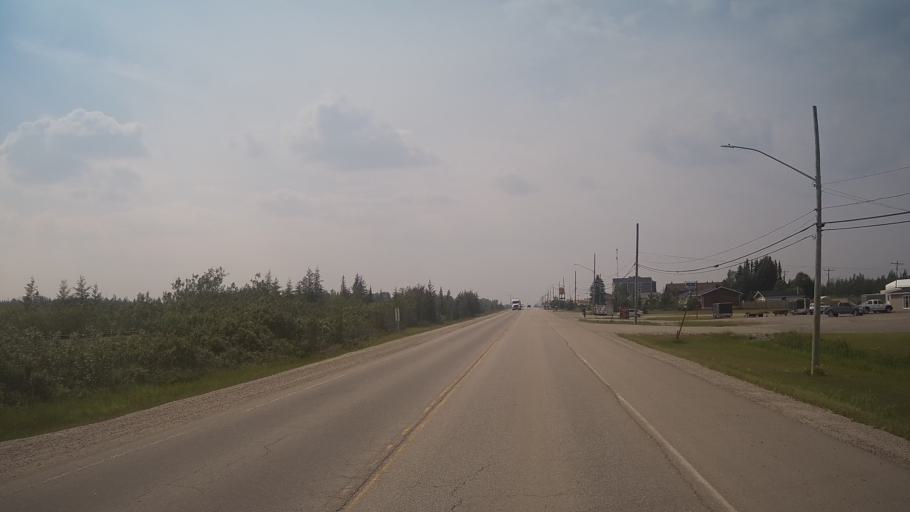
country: CA
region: Ontario
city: Kapuskasing
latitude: 49.3939
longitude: -82.3621
